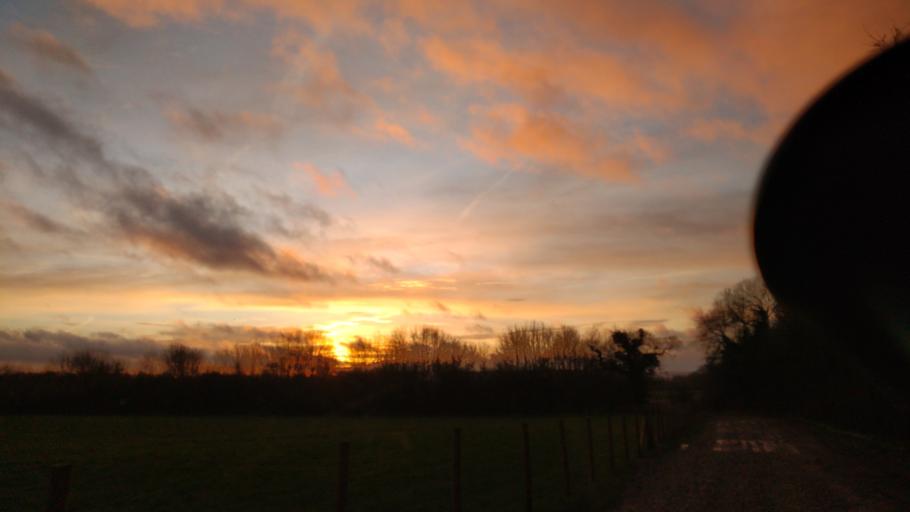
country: GB
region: England
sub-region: Oxfordshire
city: Shrivenham
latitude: 51.5916
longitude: -1.6948
